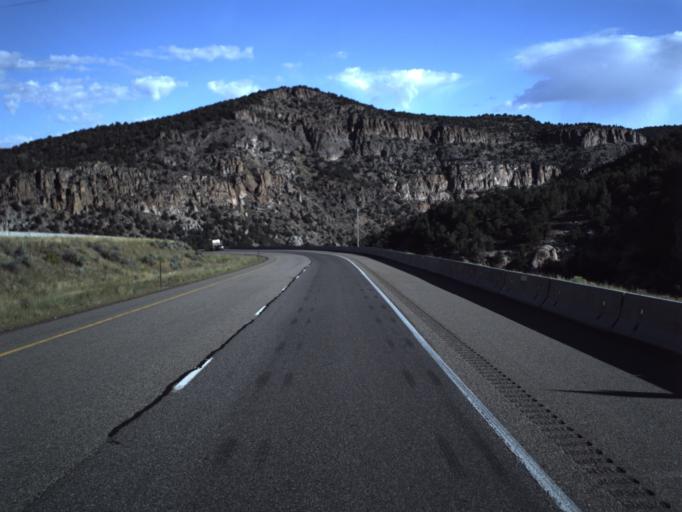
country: US
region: Utah
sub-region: Sevier County
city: Monroe
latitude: 38.5597
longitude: -112.4259
